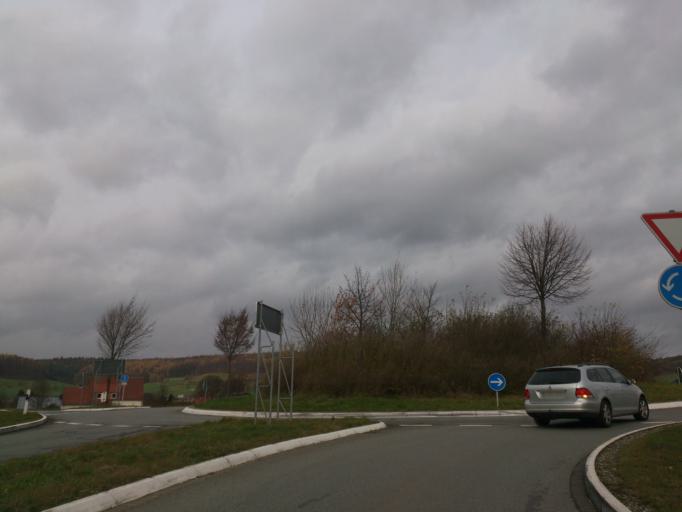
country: DE
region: North Rhine-Westphalia
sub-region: Regierungsbezirk Detmold
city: Hoexter
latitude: 51.7965
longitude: 9.3562
